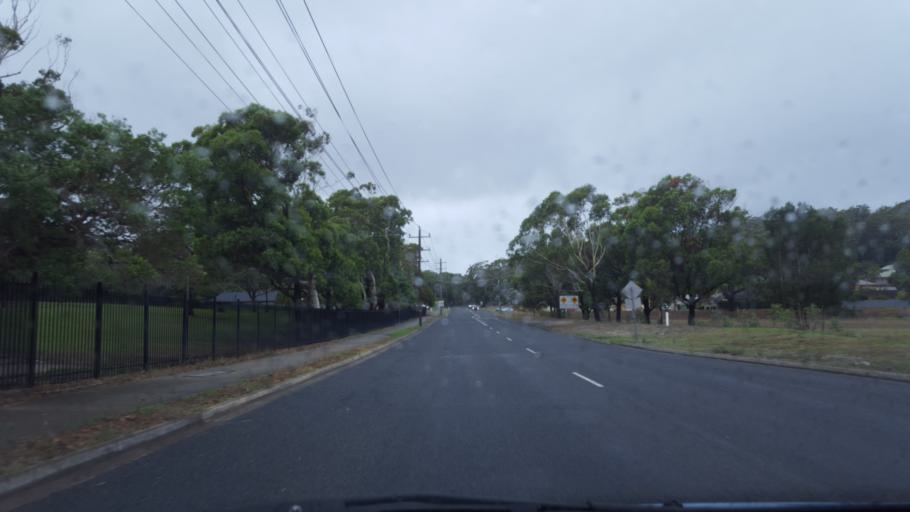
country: AU
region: New South Wales
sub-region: Port Stephens Shire
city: Anna Bay
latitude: -32.7768
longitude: 152.0903
